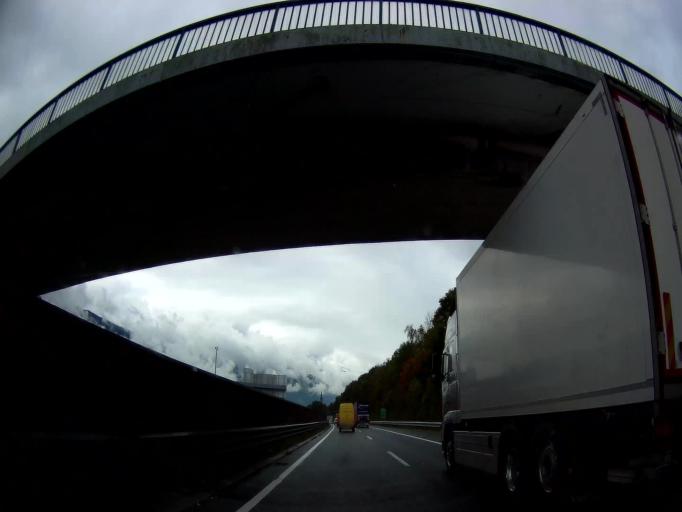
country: AT
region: Tyrol
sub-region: Politischer Bezirk Schwaz
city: Vomp
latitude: 47.3482
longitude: 11.6919
